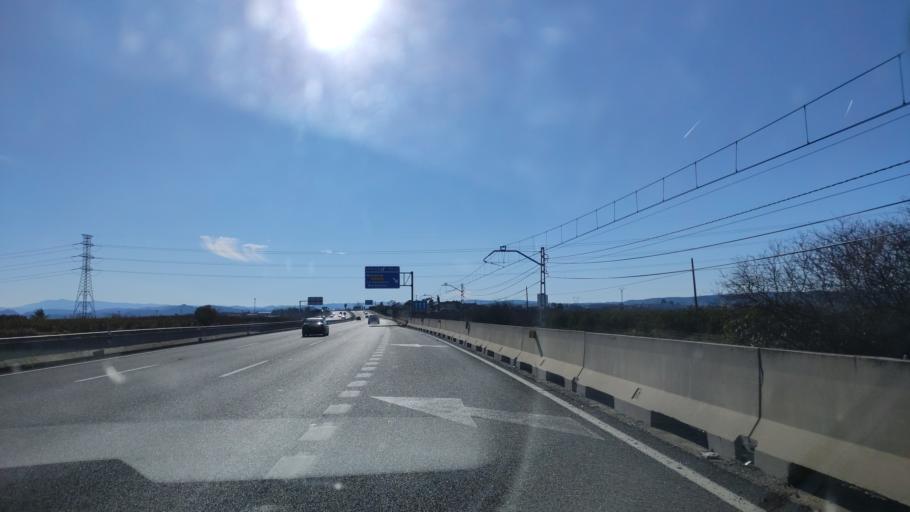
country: ES
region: Valencia
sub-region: Provincia de Valencia
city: L'Alcudia
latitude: 39.1815
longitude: -0.5133
